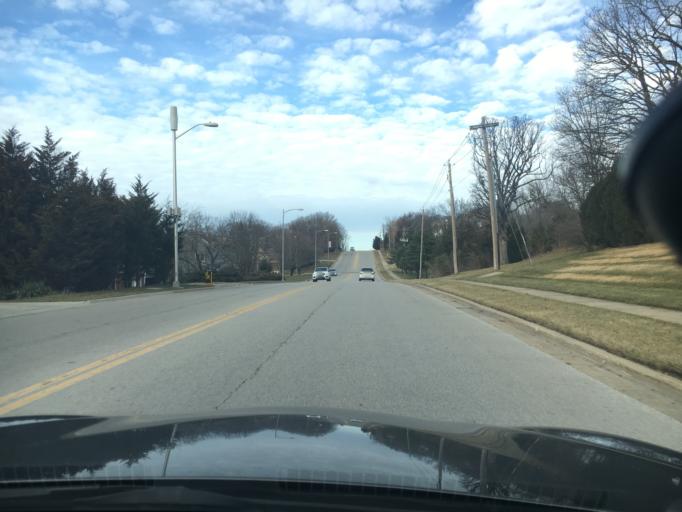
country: US
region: Kansas
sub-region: Johnson County
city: Leawood
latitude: 38.9087
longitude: -94.6305
